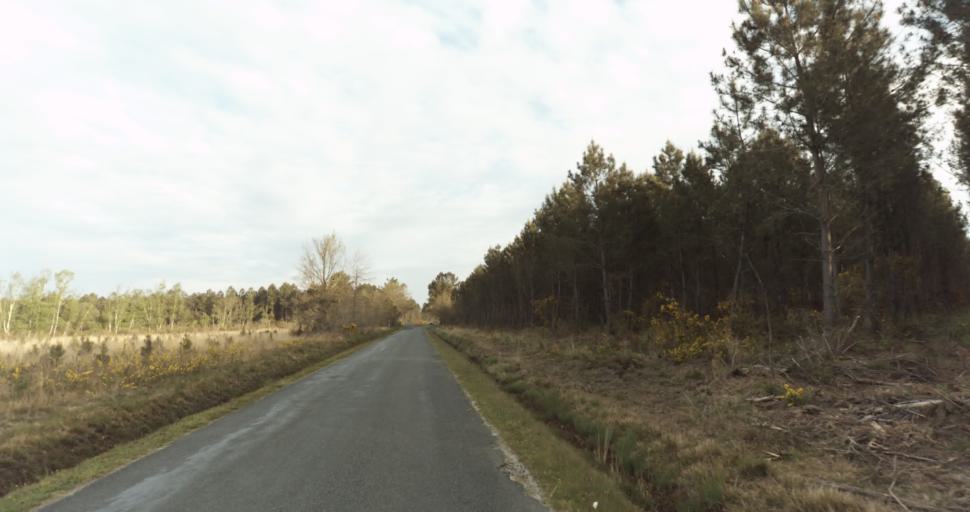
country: FR
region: Aquitaine
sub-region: Departement de la Gironde
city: Saint-Aubin-de-Medoc
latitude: 44.7895
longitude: -0.7561
